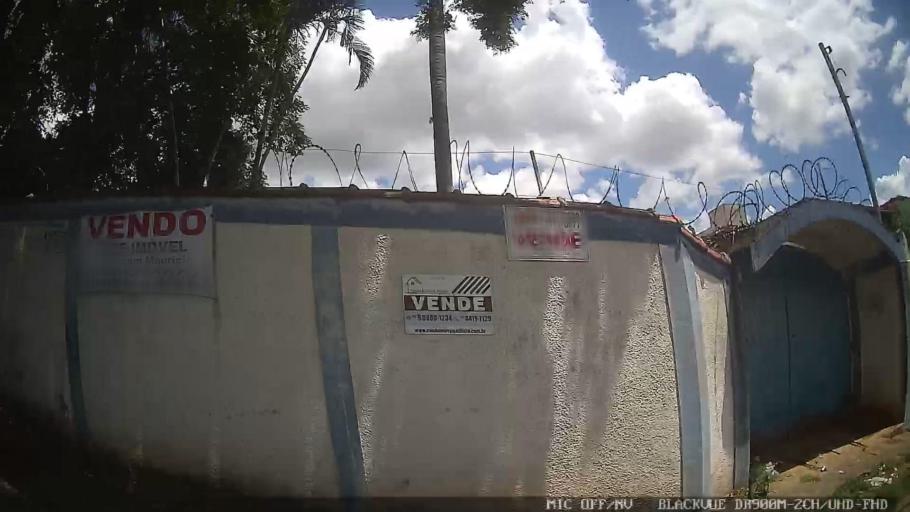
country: BR
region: Sao Paulo
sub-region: Atibaia
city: Atibaia
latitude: -23.1123
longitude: -46.5601
